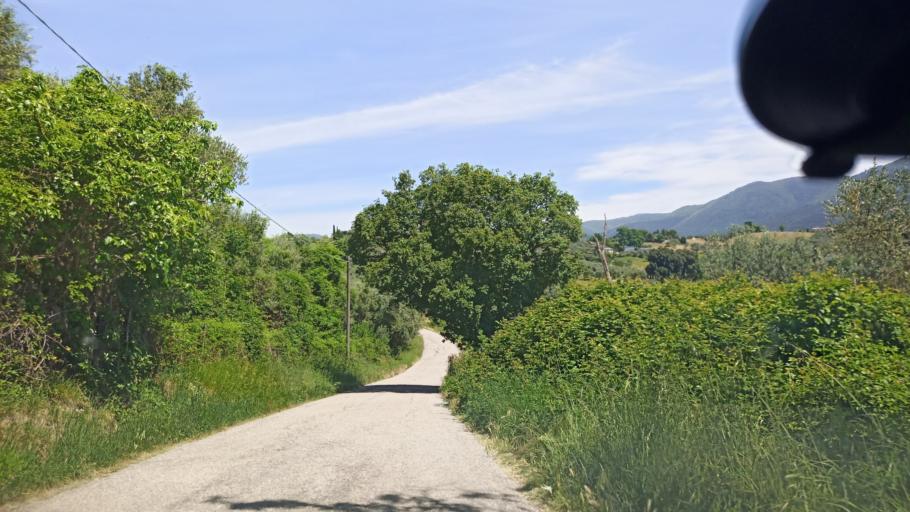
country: IT
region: Latium
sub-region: Provincia di Rieti
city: Torri in Sabina
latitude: 42.3547
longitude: 12.6337
